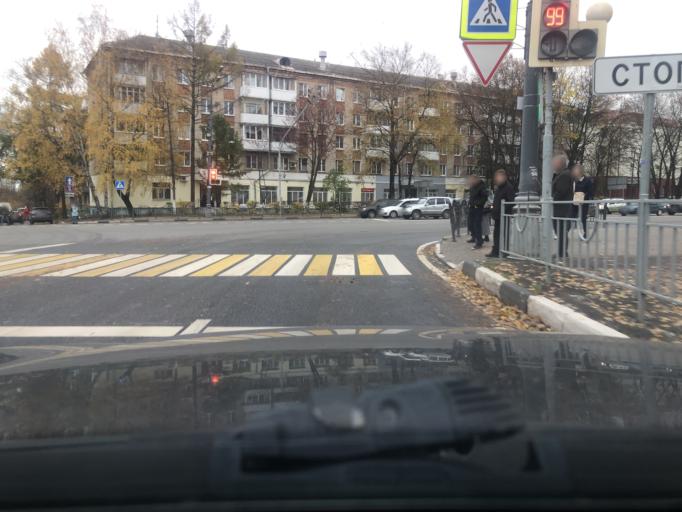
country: RU
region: Moskovskaya
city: Sergiyev Posad
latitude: 56.3197
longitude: 38.1398
